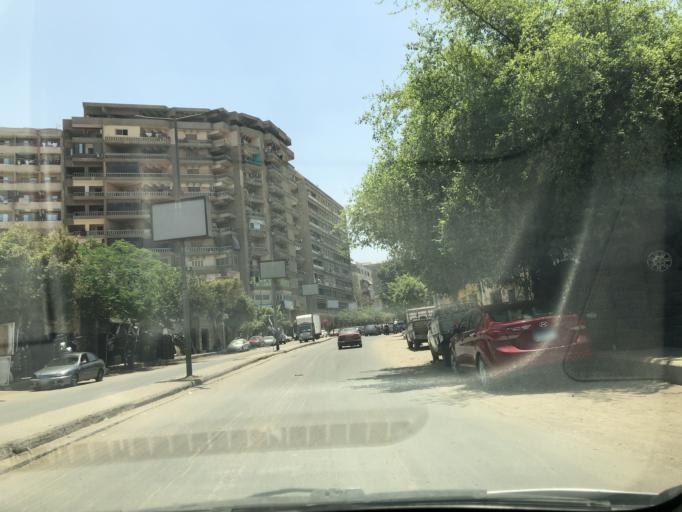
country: EG
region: Muhafazat al Qahirah
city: Cairo
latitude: 30.0657
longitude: 31.2718
